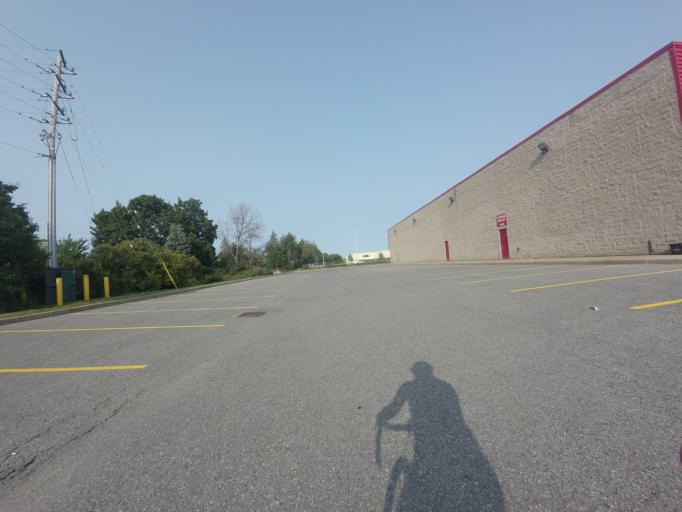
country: CA
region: Ontario
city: Ottawa
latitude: 45.3361
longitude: -75.7294
